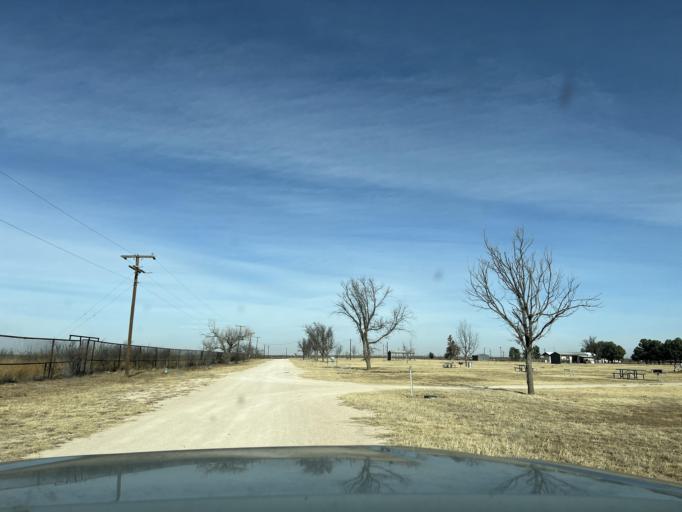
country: US
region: Texas
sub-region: Andrews County
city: Andrews
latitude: 32.4539
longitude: -102.5715
